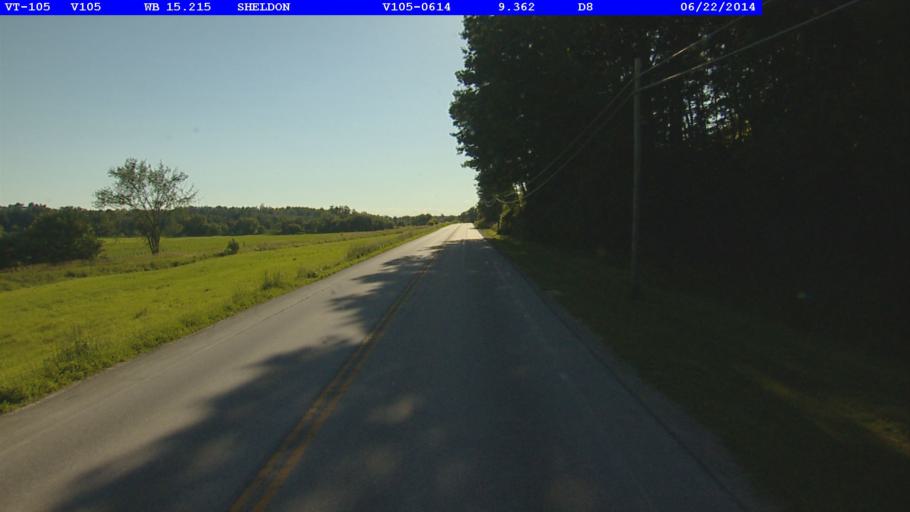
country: US
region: Vermont
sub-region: Franklin County
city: Enosburg Falls
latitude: 44.9088
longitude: -72.8531
